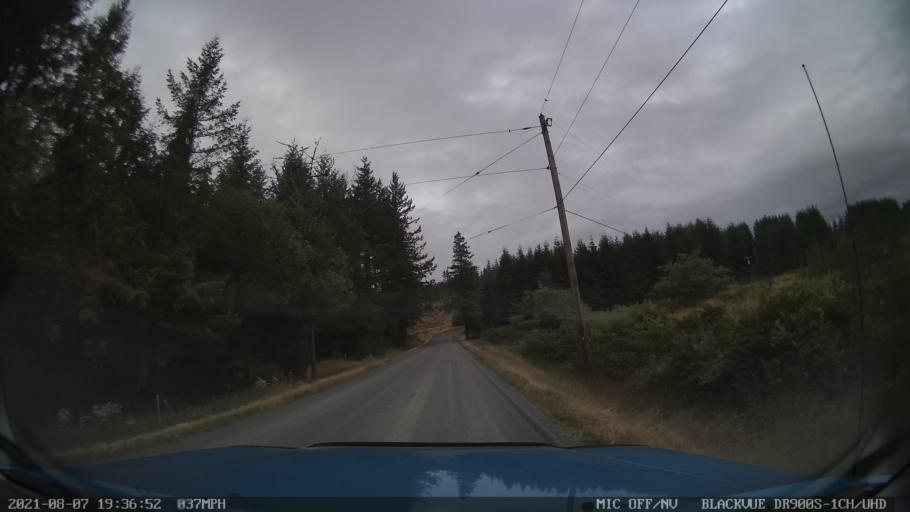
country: US
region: Oregon
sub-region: Marion County
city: Silverton
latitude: 44.9368
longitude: -122.6567
